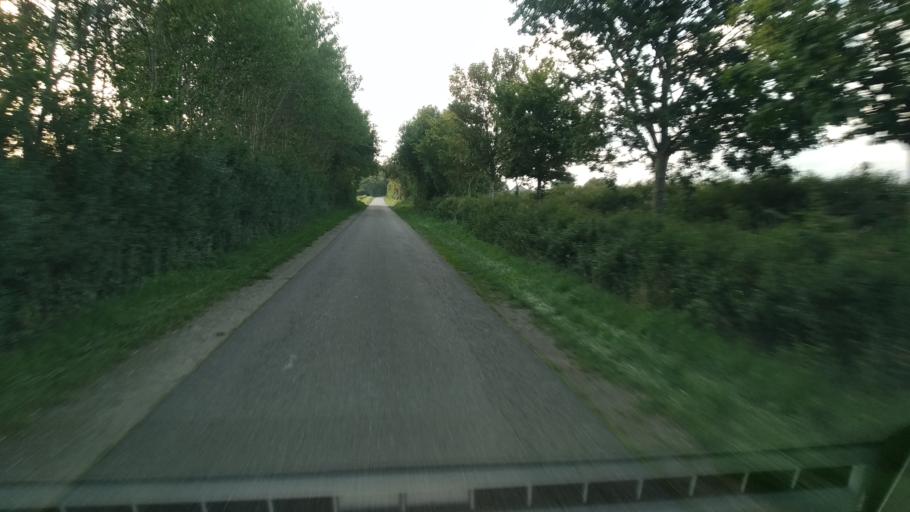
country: DE
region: Schleswig-Holstein
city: Borm
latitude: 54.4161
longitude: 9.4026
